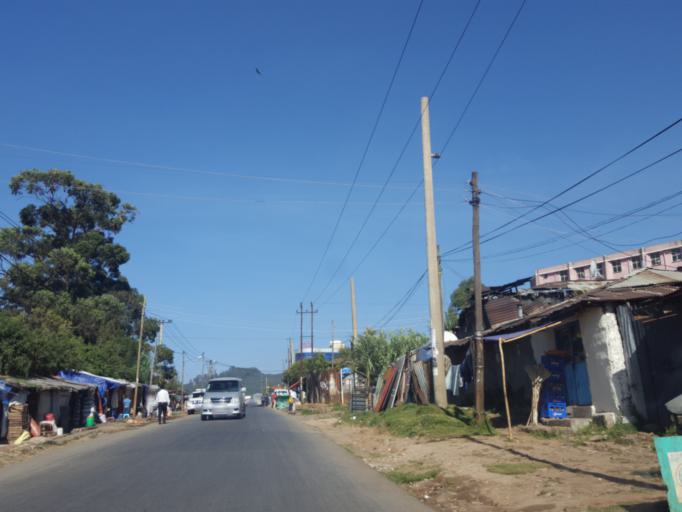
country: ET
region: Adis Abeba
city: Addis Ababa
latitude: 9.0578
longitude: 38.7289
